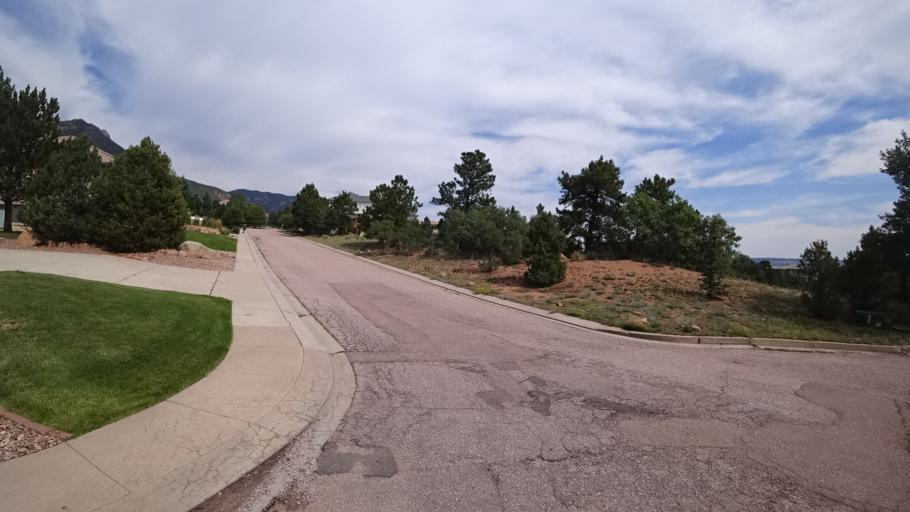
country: US
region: Colorado
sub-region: El Paso County
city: Air Force Academy
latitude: 38.9509
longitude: -104.8731
